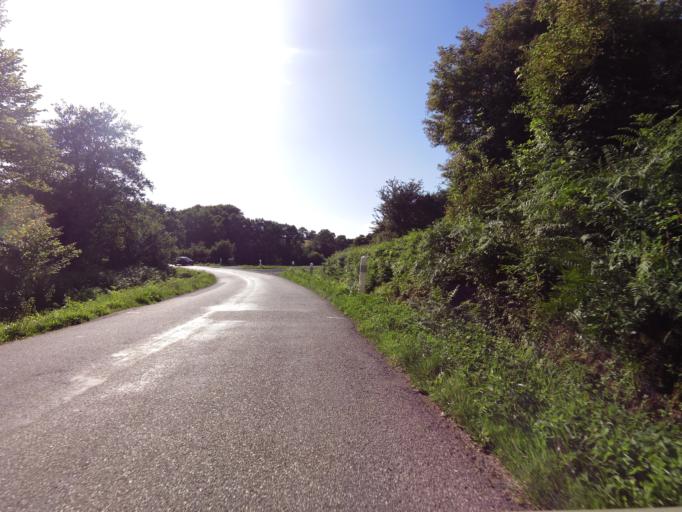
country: FR
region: Brittany
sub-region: Departement du Morbihan
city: Caden
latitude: 47.6261
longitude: -2.3117
